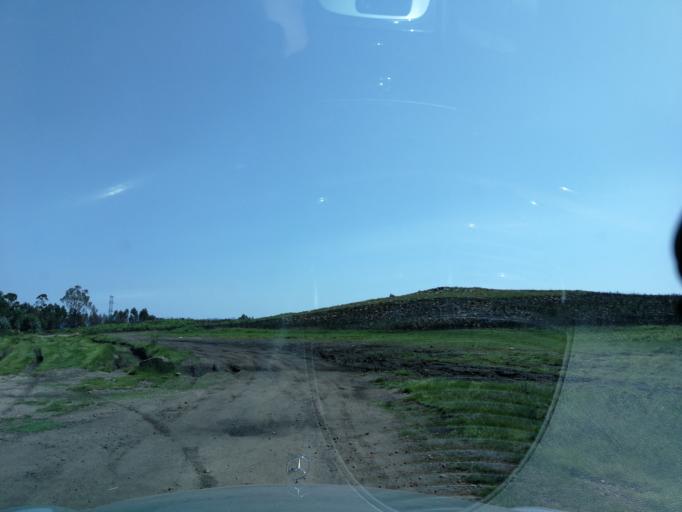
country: PT
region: Braga
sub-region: Povoa de Lanhoso
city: Povoa de Lanhoso
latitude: 41.5703
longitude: -8.3356
